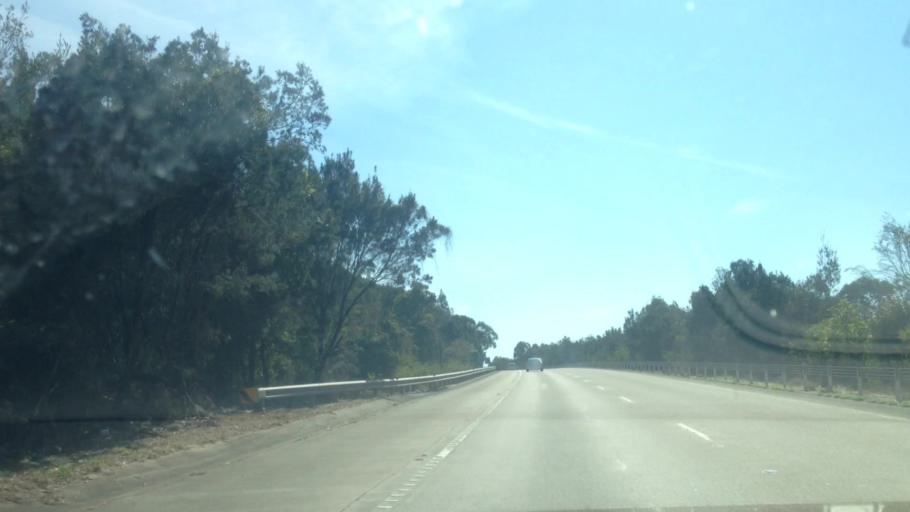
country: AU
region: New South Wales
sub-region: Lake Macquarie Shire
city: Fennell Bay
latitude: -32.9791
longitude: 151.5272
